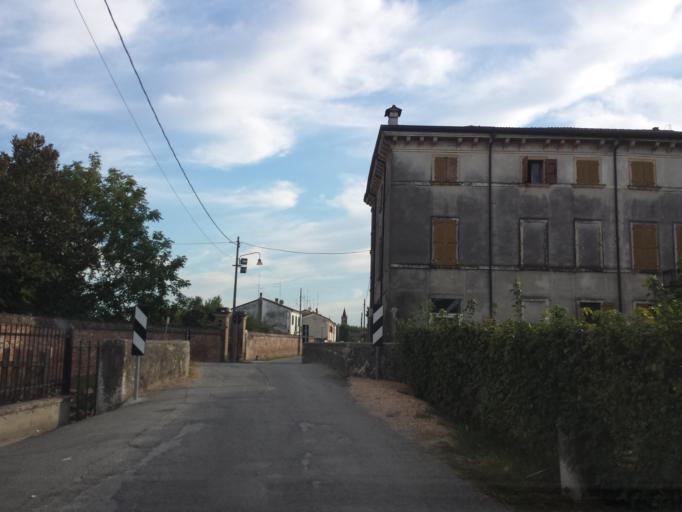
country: IT
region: Veneto
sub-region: Provincia di Verona
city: Isola della Scala
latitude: 45.2744
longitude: 10.9989
